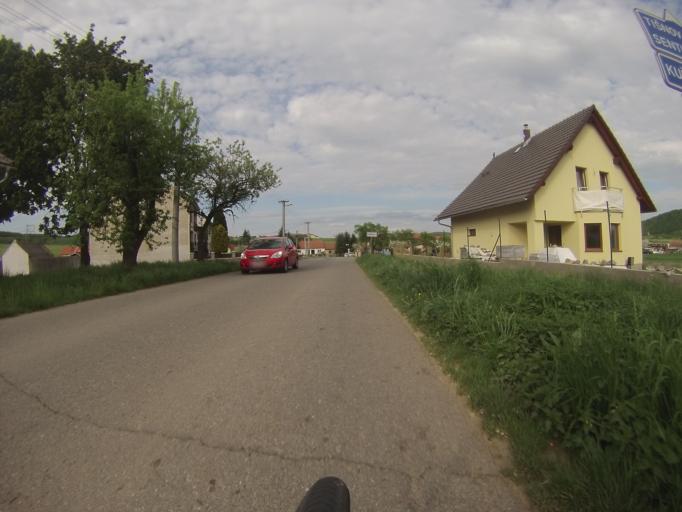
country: CZ
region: South Moravian
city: Veverska Bityska
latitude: 49.2928
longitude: 16.4526
